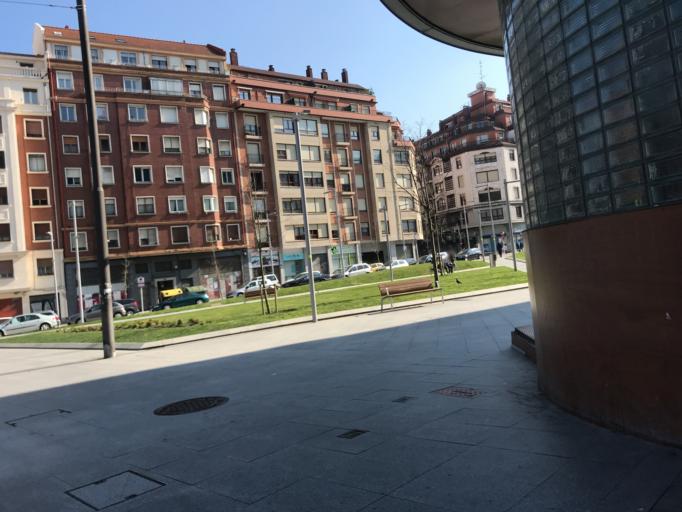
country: ES
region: Basque Country
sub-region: Bizkaia
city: Bilbao
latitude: 43.2579
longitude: -2.9487
